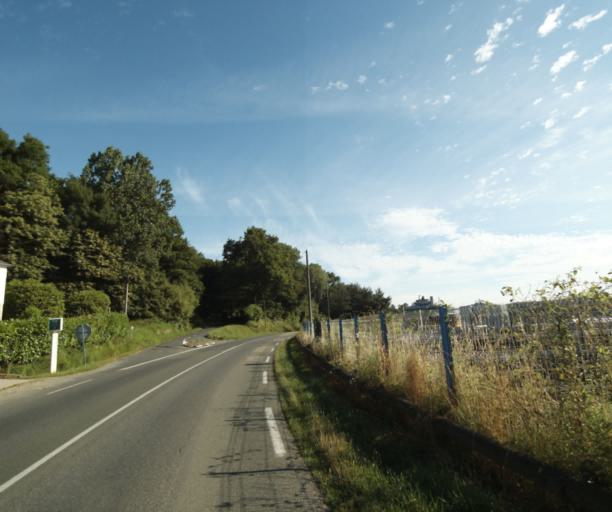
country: FR
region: Pays de la Loire
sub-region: Departement de la Mayenne
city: Laval
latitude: 48.0480
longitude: -0.7668
